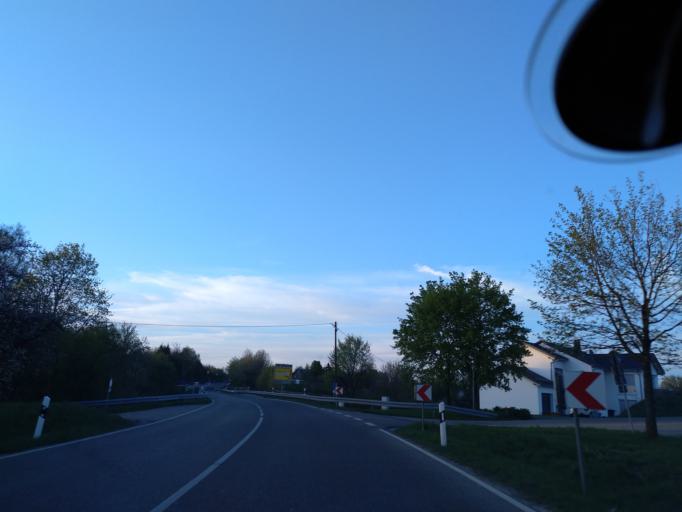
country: DE
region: Baden-Wuerttemberg
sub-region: Regierungsbezirk Stuttgart
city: Crailsheim
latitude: 49.1517
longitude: 10.0759
